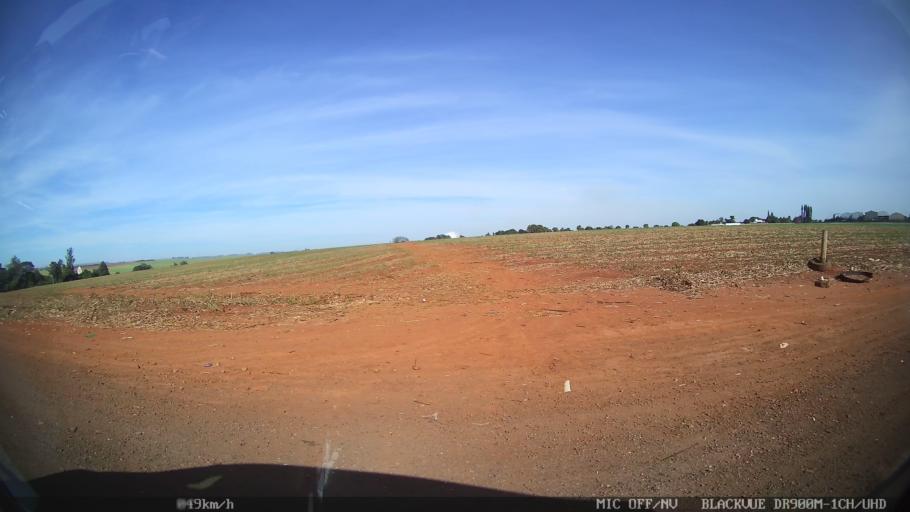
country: BR
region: Sao Paulo
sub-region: Piracicaba
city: Piracicaba
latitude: -22.7874
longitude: -47.6479
